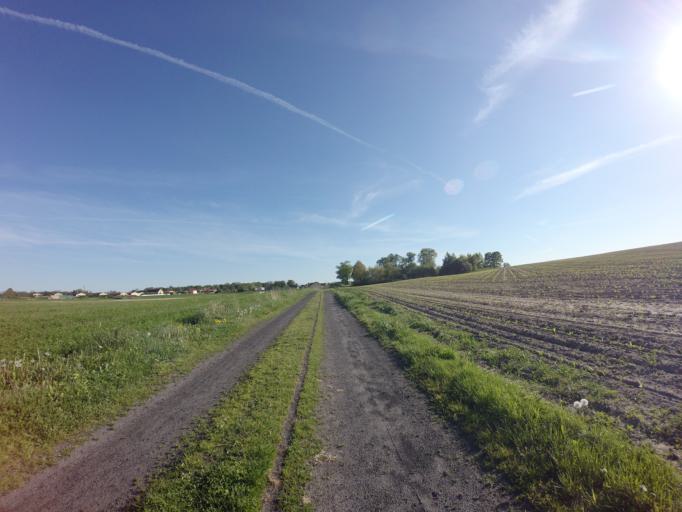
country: PL
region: West Pomeranian Voivodeship
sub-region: Powiat choszczenski
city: Pelczyce
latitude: 53.1242
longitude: 15.3232
